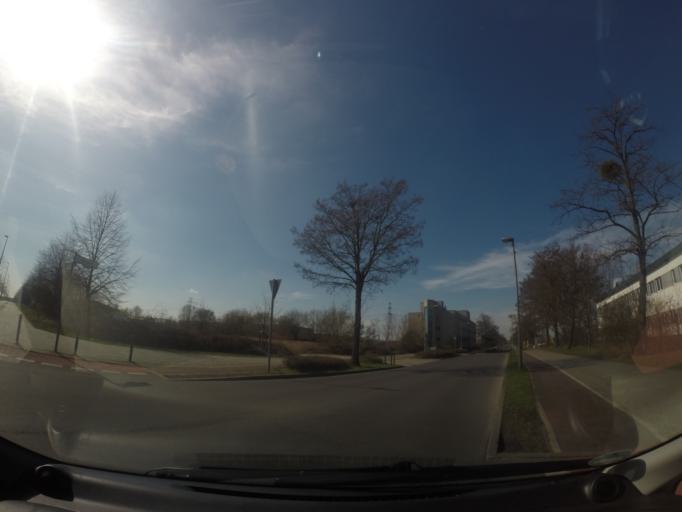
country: DE
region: Berlin
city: Falkenberg
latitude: 52.5615
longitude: 13.5518
